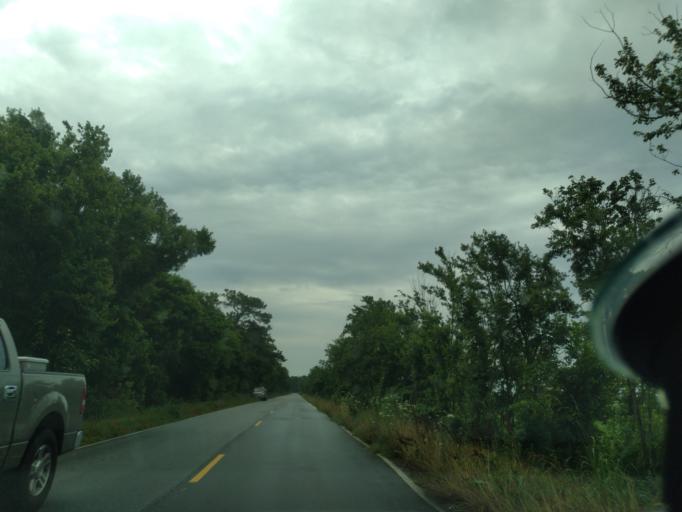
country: US
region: North Carolina
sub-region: Washington County
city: Plymouth
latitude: 35.8313
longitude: -76.5230
